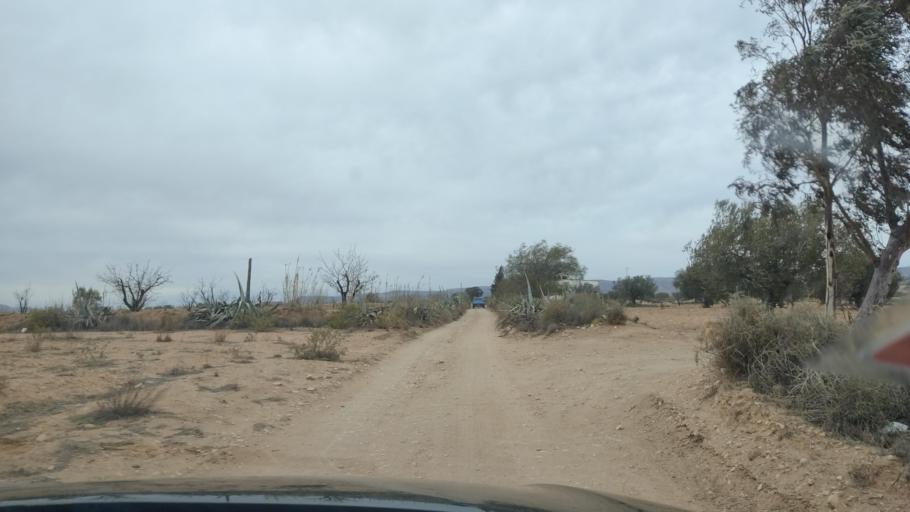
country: TN
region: Al Qasrayn
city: Kasserine
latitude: 35.2260
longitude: 8.9340
